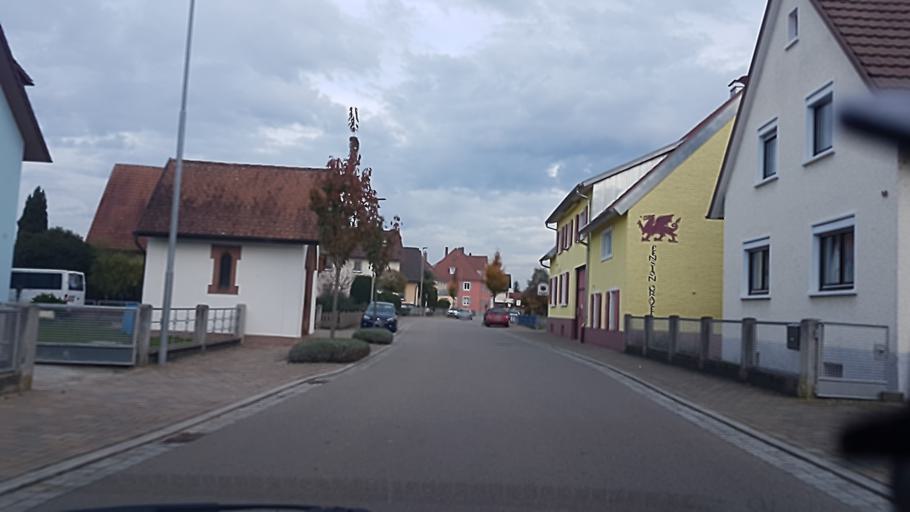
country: DE
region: Baden-Wuerttemberg
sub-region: Freiburg Region
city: Rust
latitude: 48.2676
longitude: 7.7332
